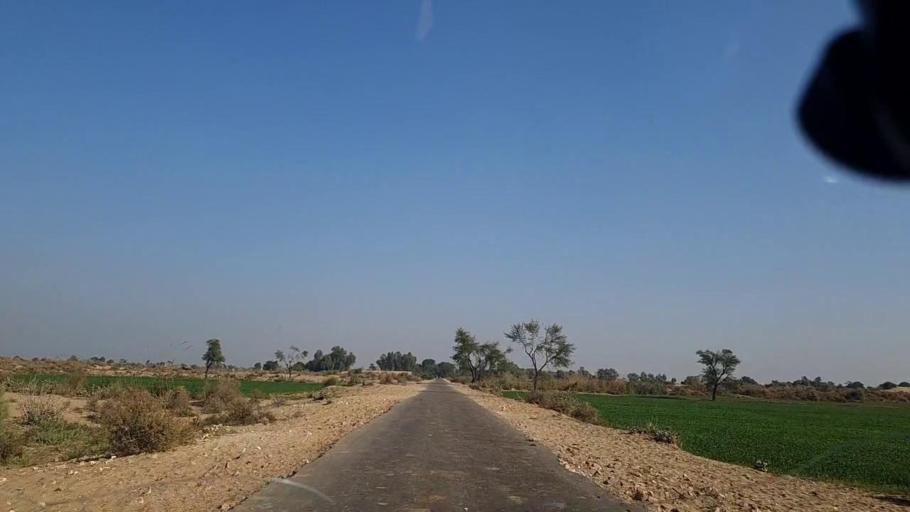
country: PK
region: Sindh
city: Khanpur
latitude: 27.6863
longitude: 69.4813
